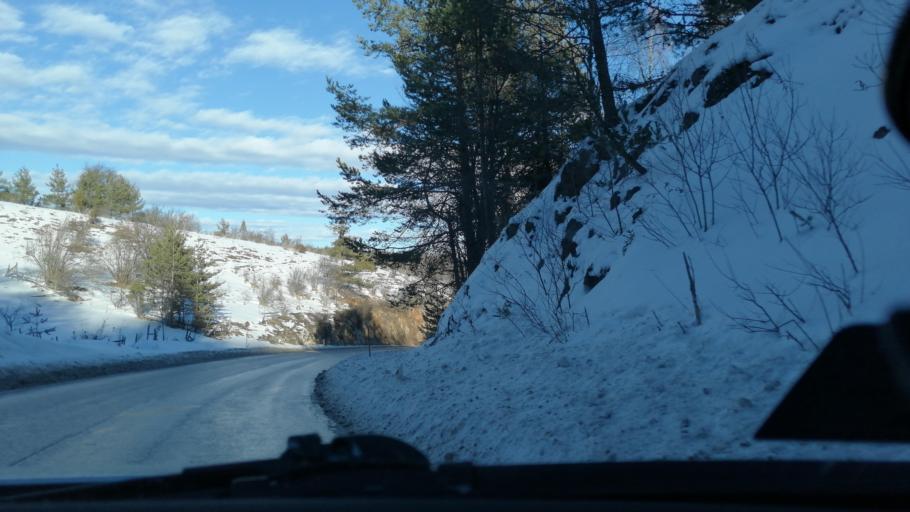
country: BA
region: Republika Srpska
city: Sokolac
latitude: 43.9167
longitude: 18.7210
